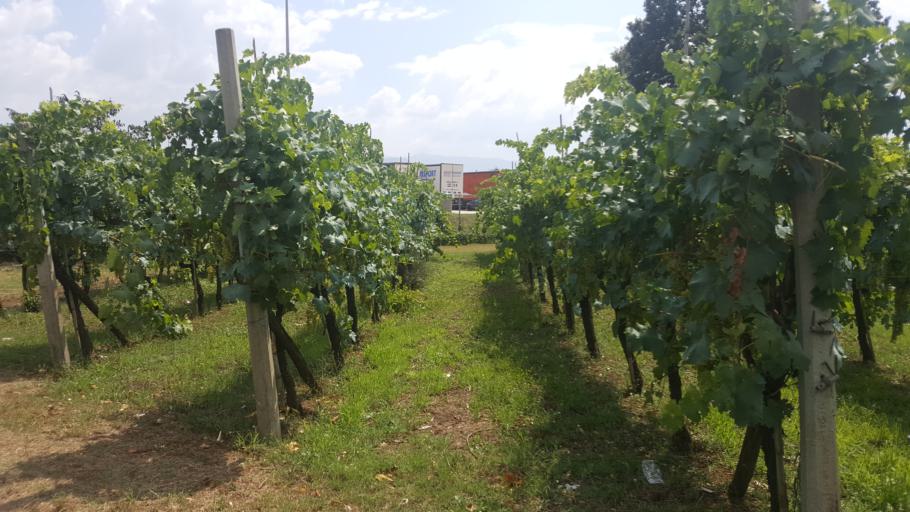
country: IT
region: Latium
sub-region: Provincia di Frosinone
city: Aquino
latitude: 41.4989
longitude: 13.6828
